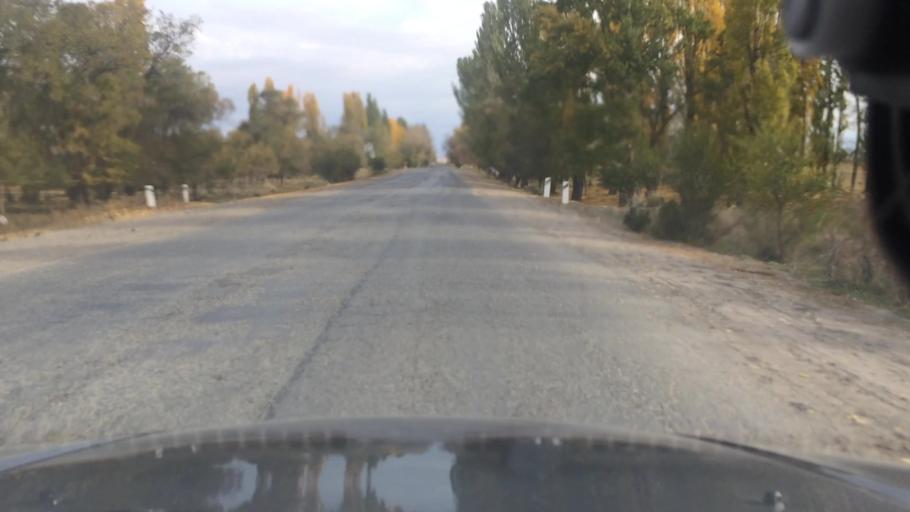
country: KG
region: Ysyk-Koel
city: Karakol
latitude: 42.5405
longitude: 78.3843
